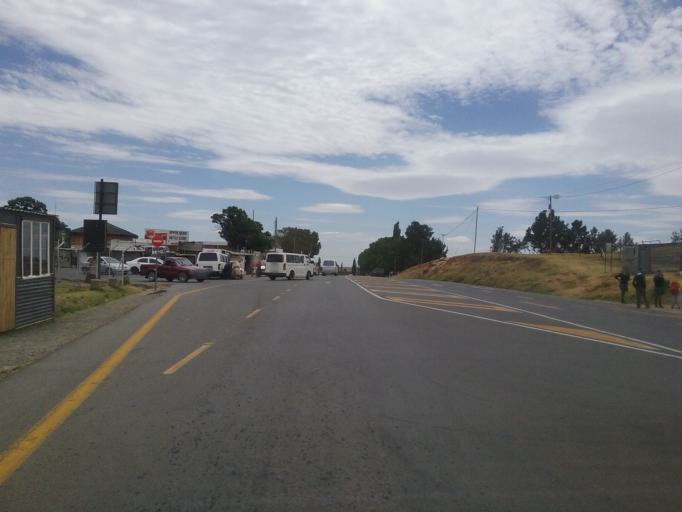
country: LS
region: Maseru
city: Maseru
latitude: -29.4884
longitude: 27.5271
